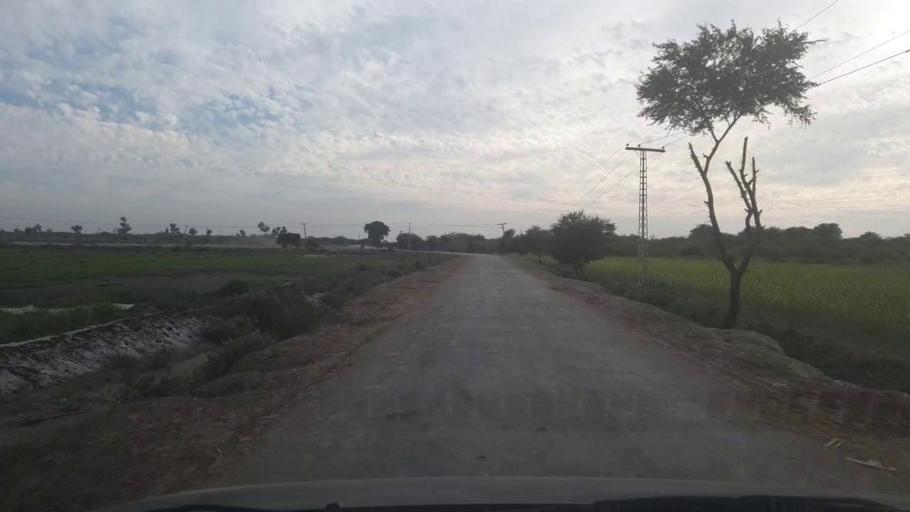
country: PK
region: Sindh
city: Samaro
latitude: 25.3238
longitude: 69.2354
